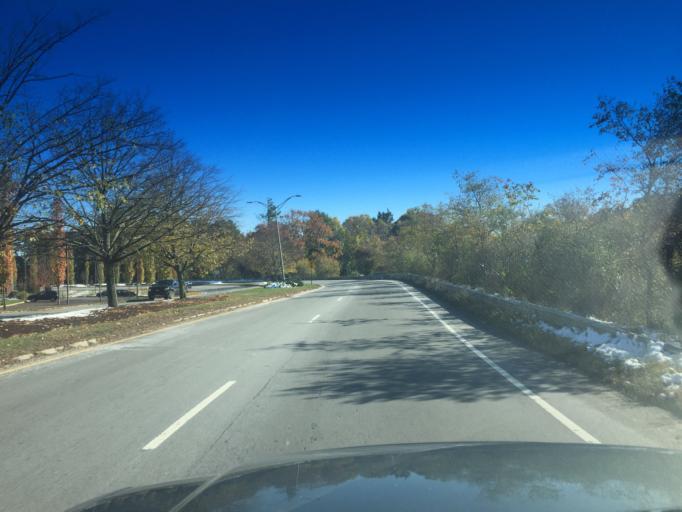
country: US
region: Massachusetts
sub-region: Bristol County
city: Raynham
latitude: 41.9600
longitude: -71.1231
